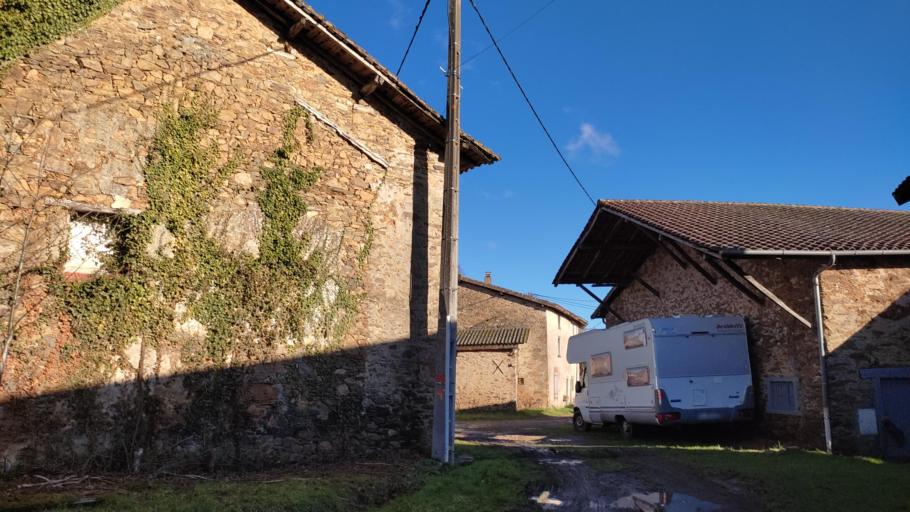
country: FR
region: Limousin
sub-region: Departement de la Haute-Vienne
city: Isle
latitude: 45.8115
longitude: 1.1836
